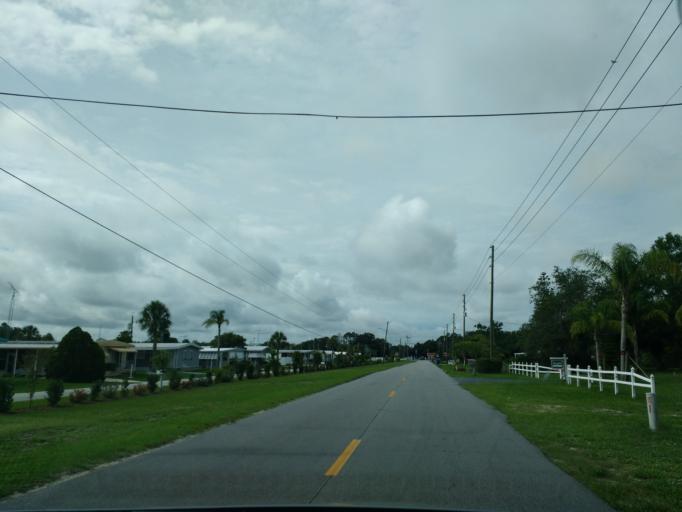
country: US
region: Florida
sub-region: Highlands County
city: Sebring
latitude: 27.4738
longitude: -81.4862
